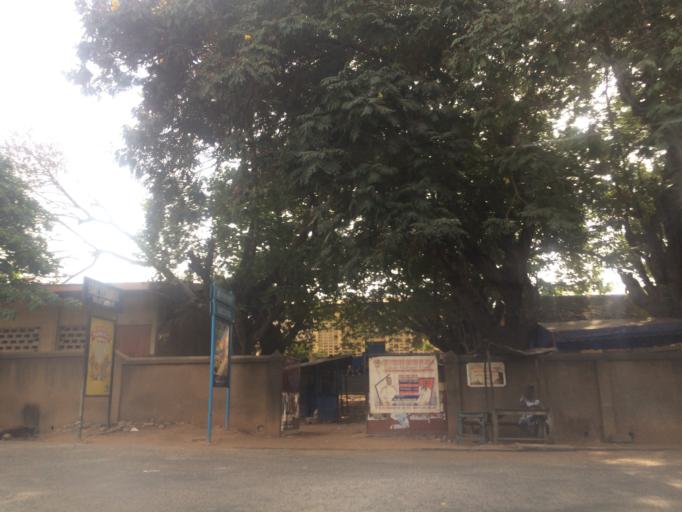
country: GH
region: Greater Accra
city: Accra
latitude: 5.5624
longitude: -0.2101
